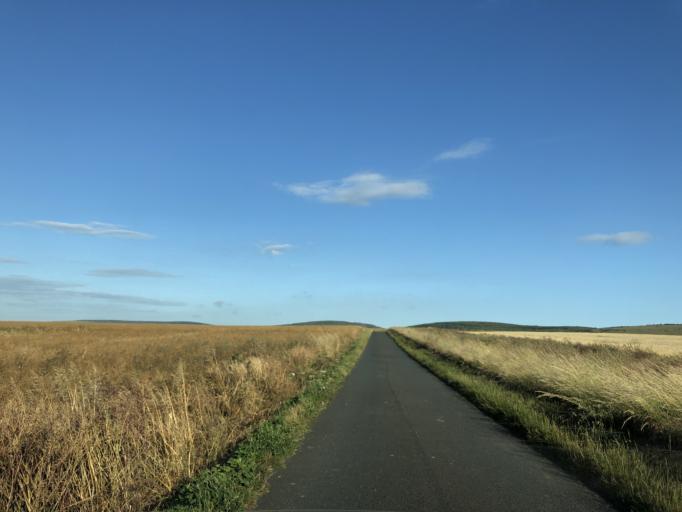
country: GB
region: England
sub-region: Isle of Wight
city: Yarmouth
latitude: 50.6836
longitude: -1.4677
